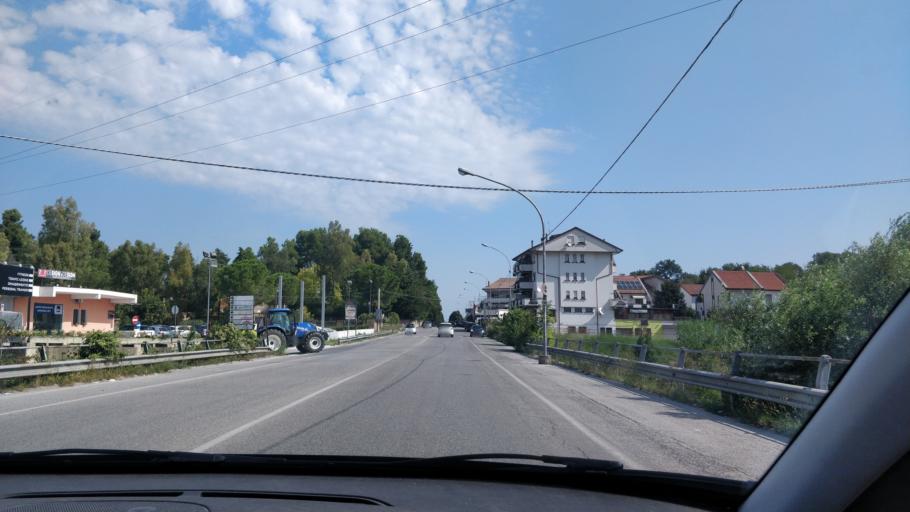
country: IT
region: Abruzzo
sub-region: Provincia di Chieti
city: Chieti
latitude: 42.3859
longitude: 14.1549
